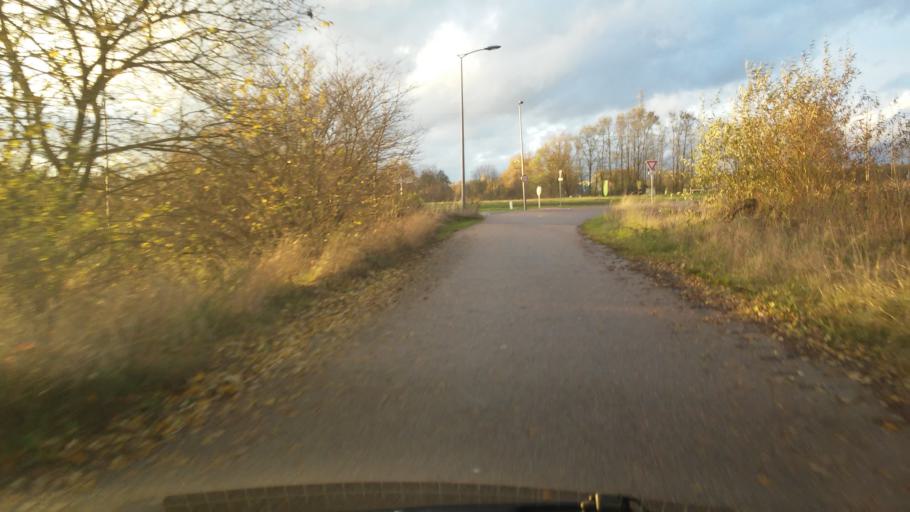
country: FR
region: Lorraine
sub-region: Departement de la Moselle
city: Talange
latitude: 49.2371
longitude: 6.1845
